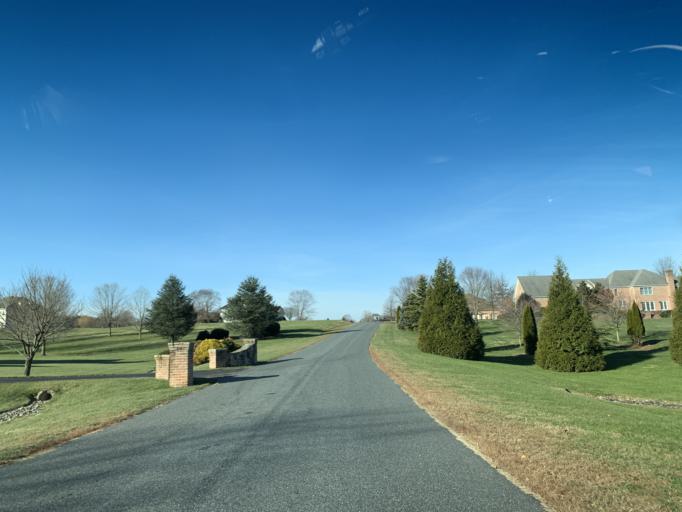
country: US
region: Maryland
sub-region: Harford County
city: Bel Air South
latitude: 39.5686
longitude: -76.2494
